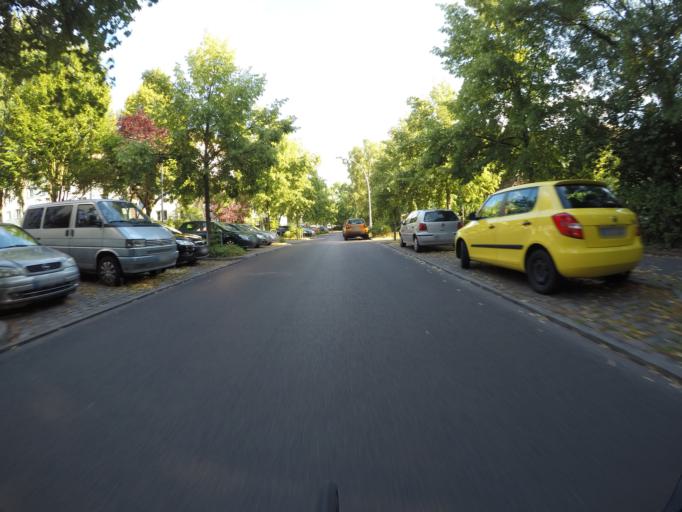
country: DE
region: Berlin
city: Weissensee
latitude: 52.5568
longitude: 13.4784
